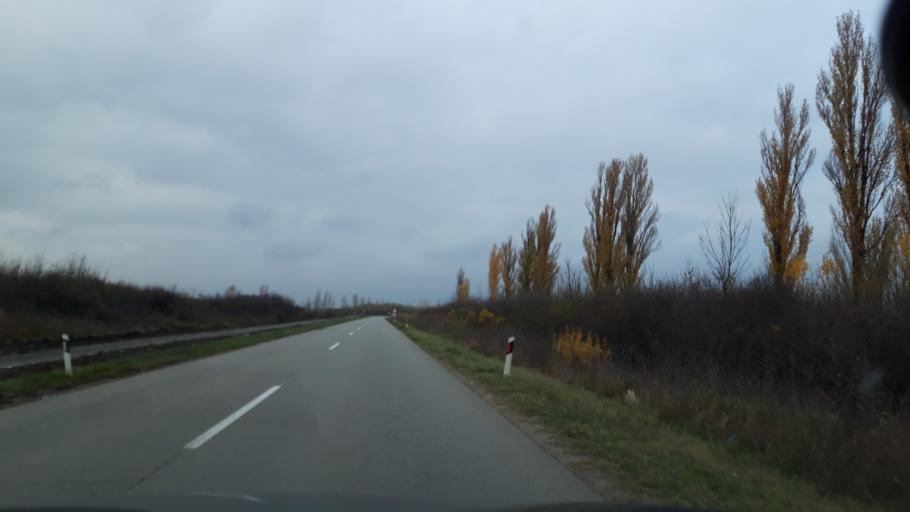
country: RS
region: Autonomna Pokrajina Vojvodina
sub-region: Severnobanatski Okrug
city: Novi Knezevac
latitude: 46.0731
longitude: 20.1033
